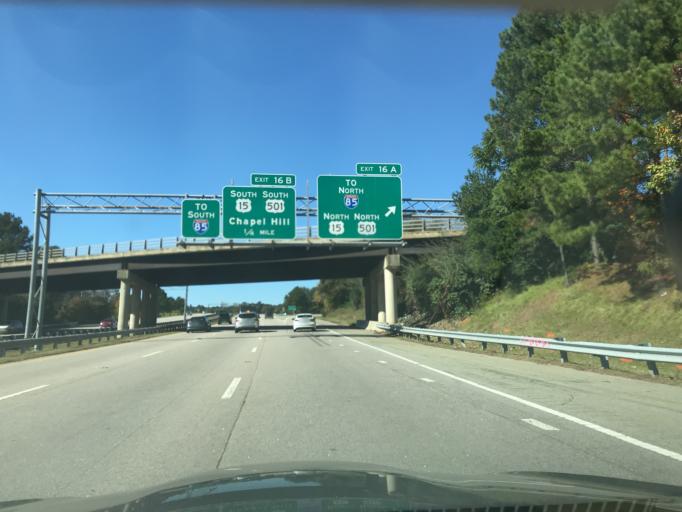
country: US
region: North Carolina
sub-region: Durham County
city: Durham
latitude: 36.0161
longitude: -78.9452
